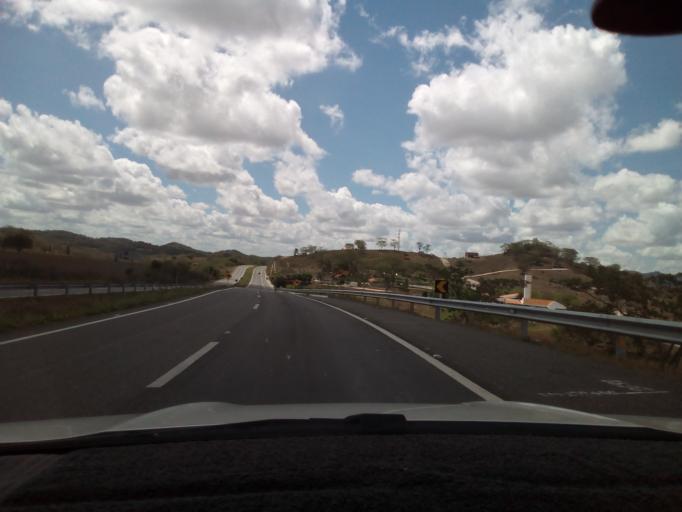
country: BR
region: Paraiba
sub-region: Massaranduba
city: Massaranduba
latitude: -7.2682
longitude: -35.7989
